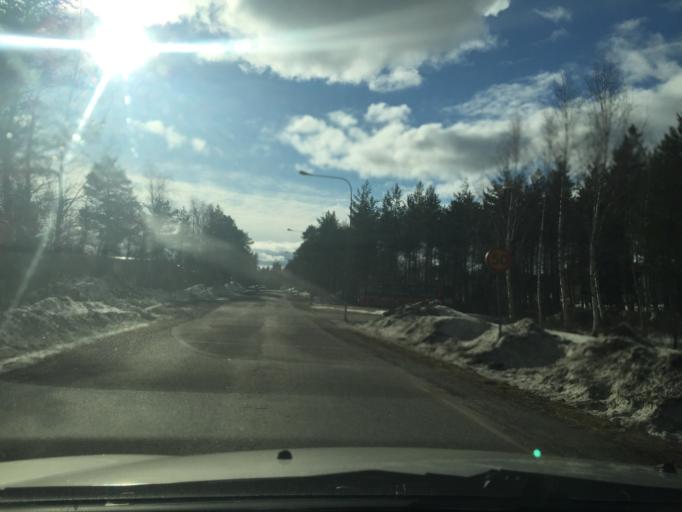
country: SE
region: Norrbotten
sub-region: Lulea Kommun
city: Lulea
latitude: 65.5947
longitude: 22.2419
